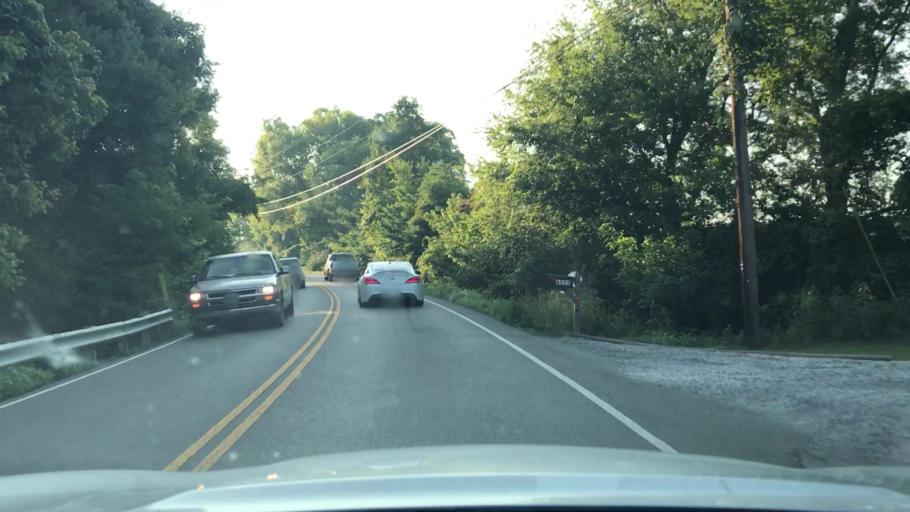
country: US
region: Tennessee
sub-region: Williamson County
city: Nolensville
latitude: 35.9900
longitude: -86.6383
